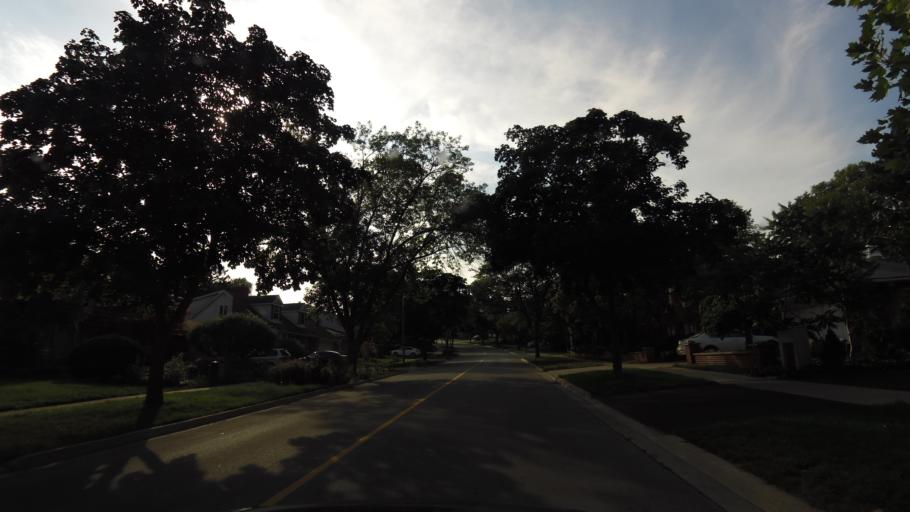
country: CA
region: Ontario
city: Burlington
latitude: 43.3453
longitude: -79.8468
